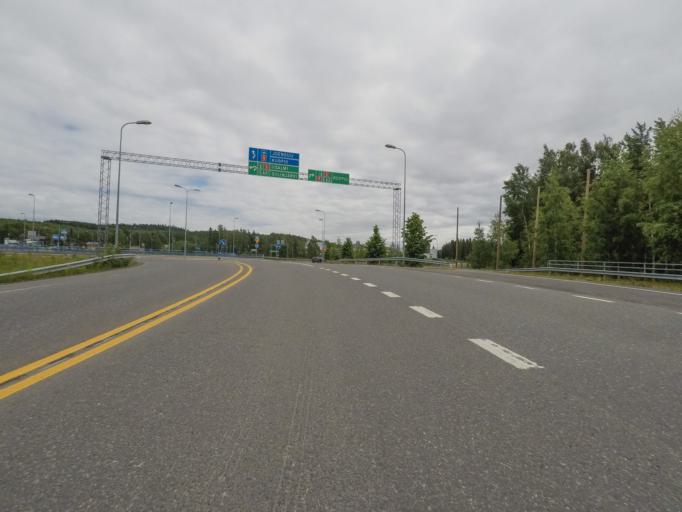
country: FI
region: Northern Savo
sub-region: Kuopio
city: Kuopio
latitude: 62.9730
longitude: 27.7035
